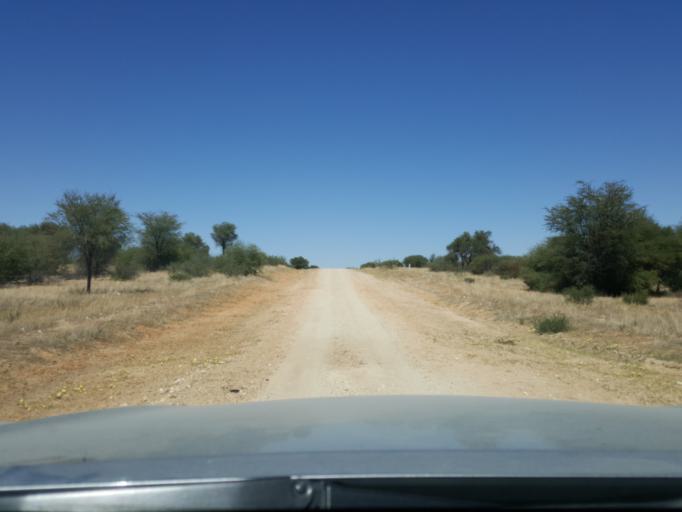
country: BW
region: Kgalagadi
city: Hukuntsi
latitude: -24.0469
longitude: 21.2205
